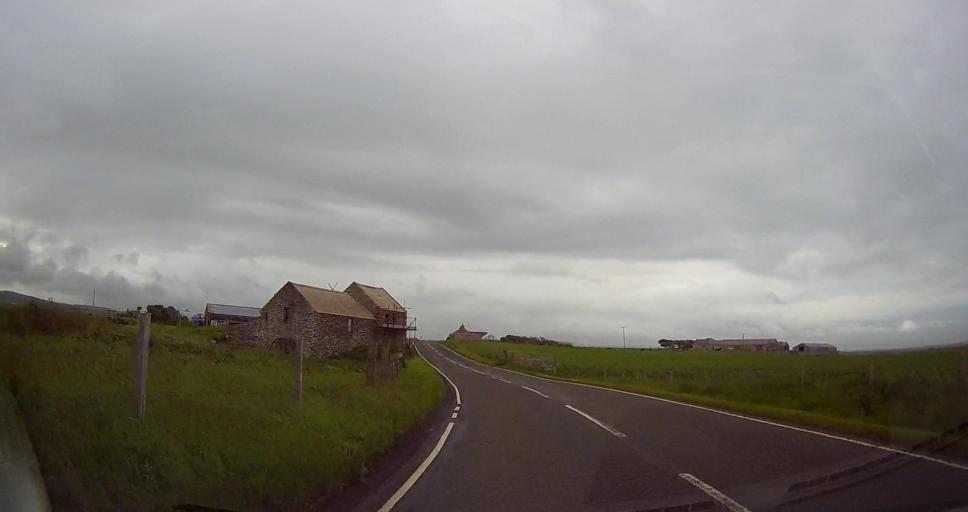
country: GB
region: Scotland
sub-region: Orkney Islands
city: Stromness
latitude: 59.0771
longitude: -3.2506
